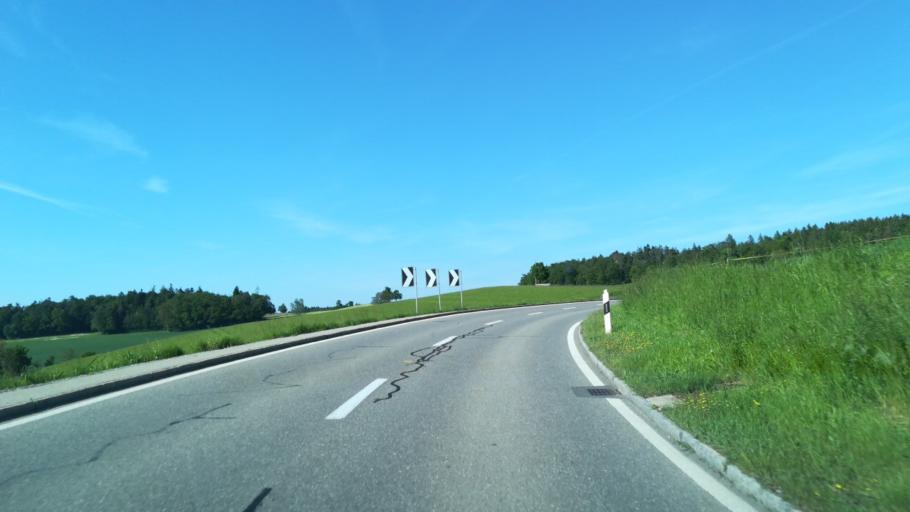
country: CH
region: Zurich
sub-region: Bezirk Andelfingen
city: Kleinandelfingen
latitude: 47.6162
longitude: 8.7343
